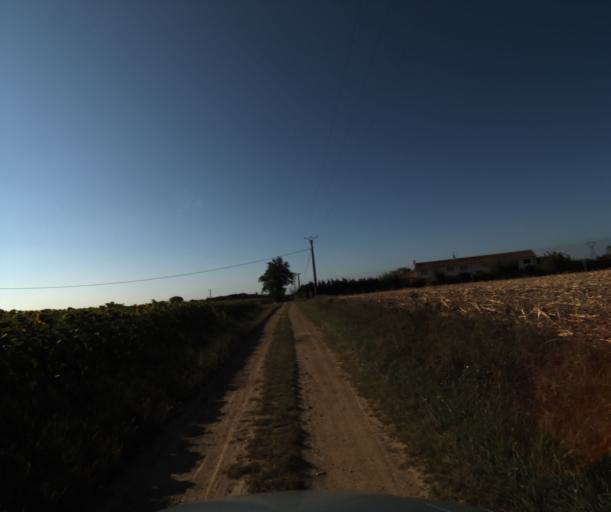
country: FR
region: Midi-Pyrenees
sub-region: Departement de la Haute-Garonne
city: Labarthe-sur-Leze
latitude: 43.4457
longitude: 1.3741
